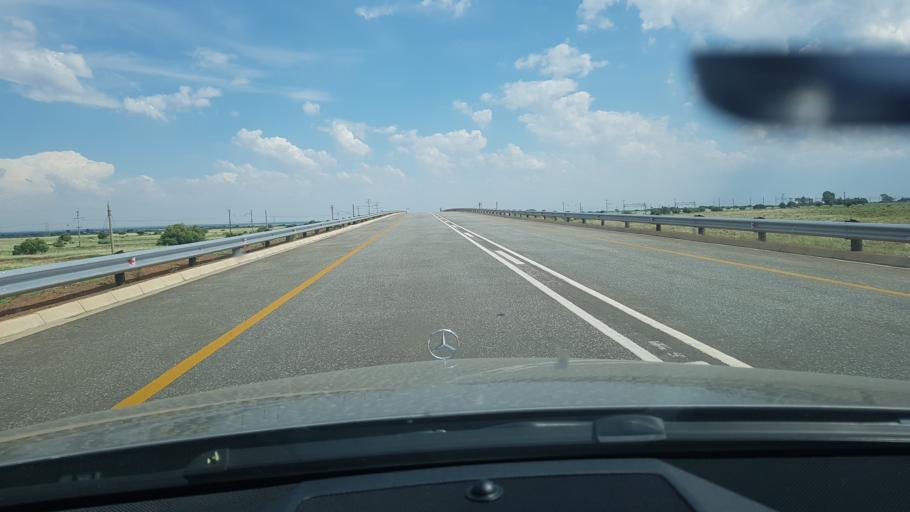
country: ZA
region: North-West
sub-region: Dr Ruth Segomotsi Mompati District Municipality
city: Bloemhof
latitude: -27.5481
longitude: 25.6980
